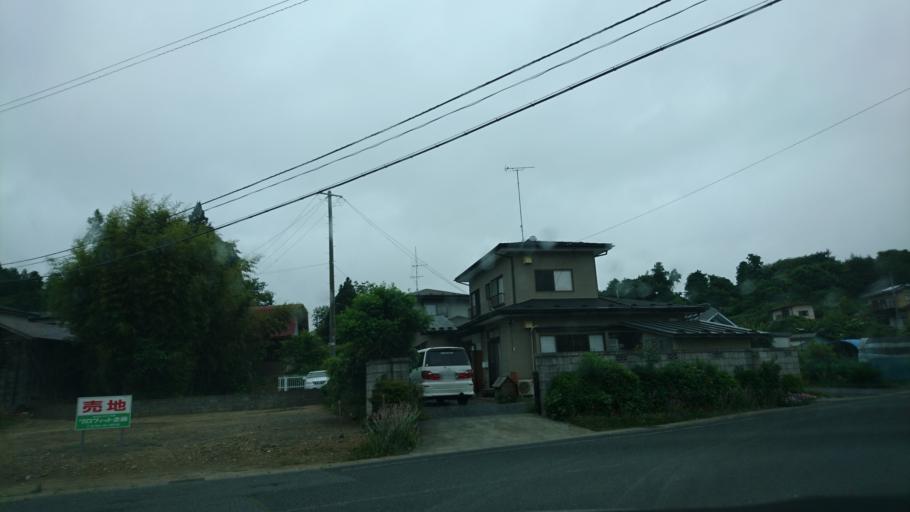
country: JP
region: Iwate
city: Ichinoseki
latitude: 38.9324
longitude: 141.1725
